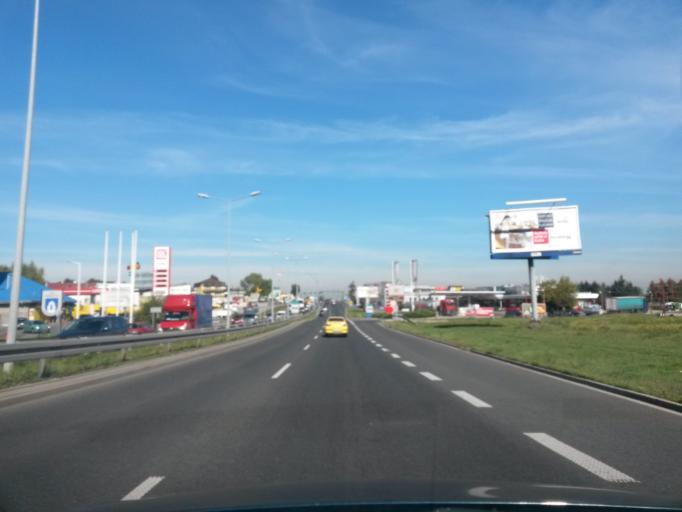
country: PL
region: Lesser Poland Voivodeship
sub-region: Powiat krakowski
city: Libertow
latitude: 49.9803
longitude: 19.9109
